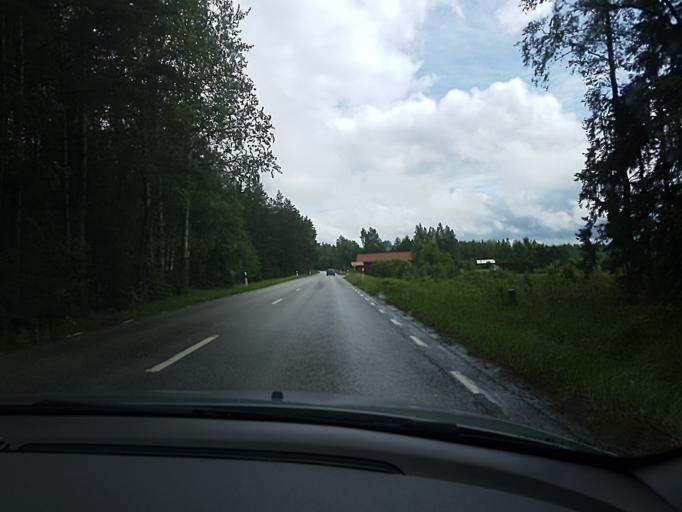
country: SE
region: Uppsala
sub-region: Osthammars Kommun
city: OEsthammar
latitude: 60.2778
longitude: 18.3016
